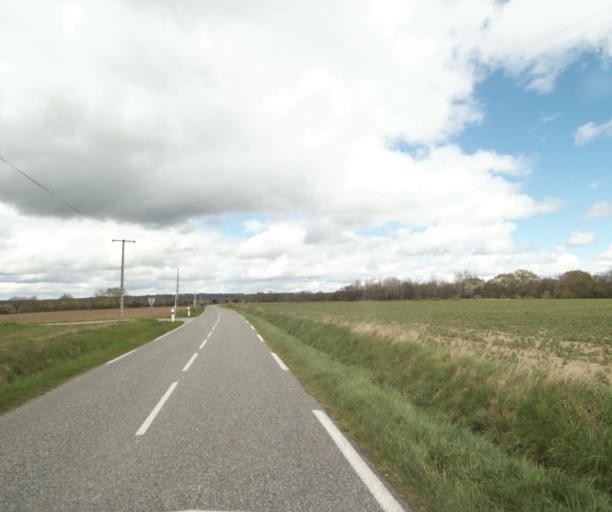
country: FR
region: Midi-Pyrenees
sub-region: Departement de la Haute-Garonne
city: Calmont
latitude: 43.2535
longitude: 1.6371
